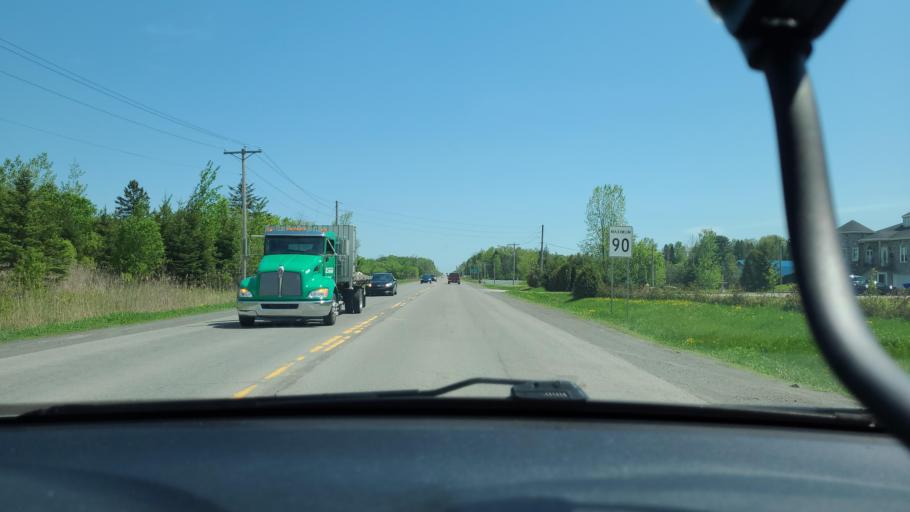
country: CA
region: Quebec
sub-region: Laurentides
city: Saint-Colomban
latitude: 45.6728
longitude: -74.1808
